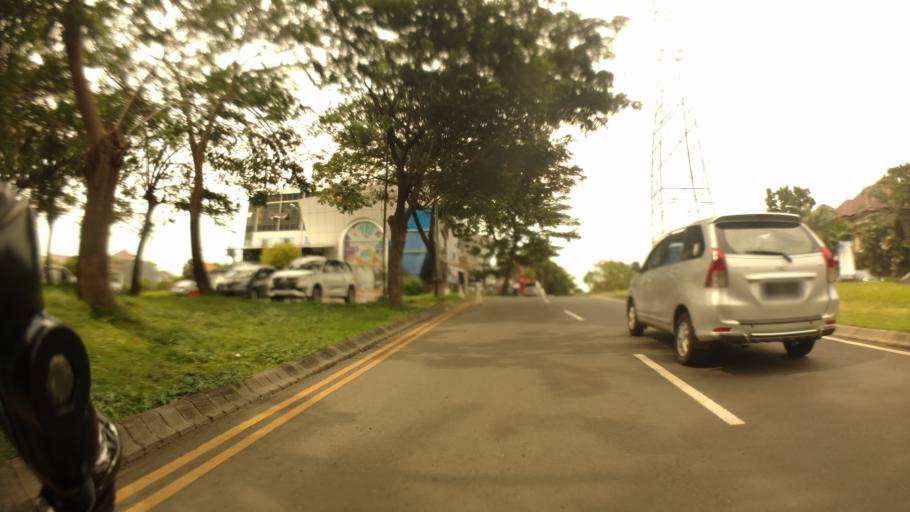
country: ID
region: East Java
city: Driyorejo
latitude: -7.2919
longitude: 112.6483
